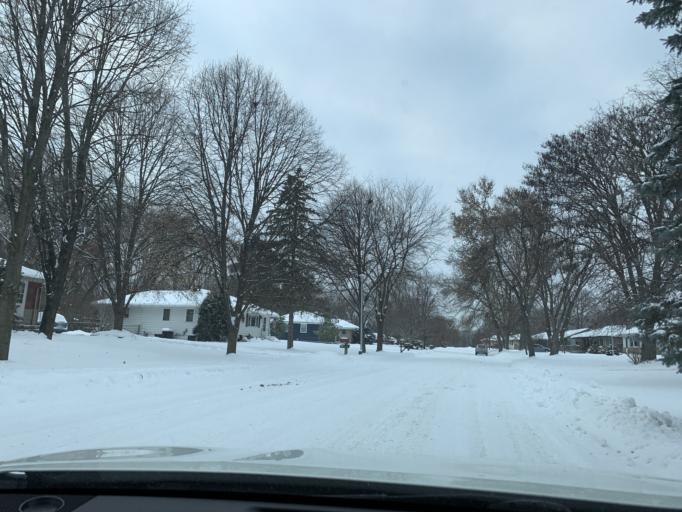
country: US
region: Minnesota
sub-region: Anoka County
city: Coon Rapids
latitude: 45.1722
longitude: -93.2881
